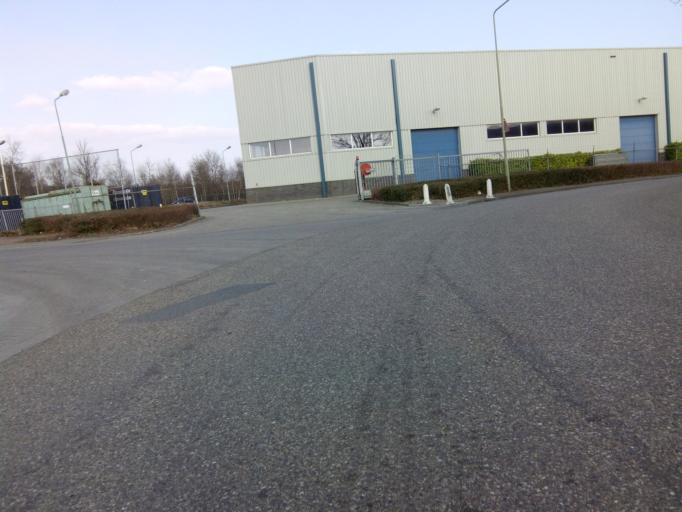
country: NL
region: Utrecht
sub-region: Gemeente Utrechtse Heuvelrug
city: Overberg
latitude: 52.0858
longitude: 5.4719
